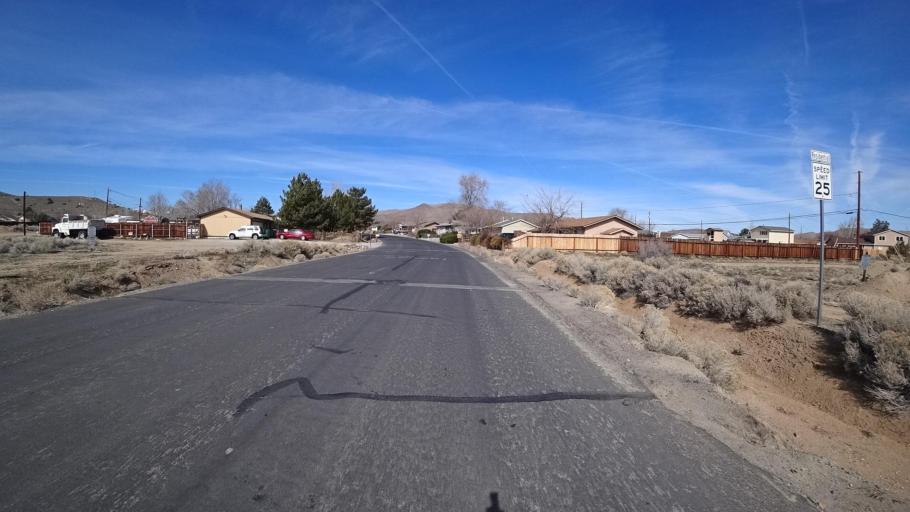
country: US
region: Nevada
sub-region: Washoe County
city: Spanish Springs
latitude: 39.6278
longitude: -119.7209
